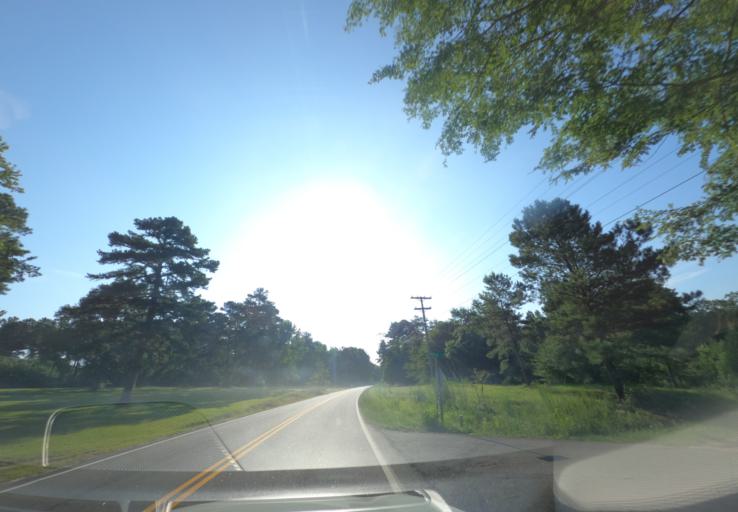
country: US
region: South Carolina
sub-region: Edgefield County
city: Murphys Estates
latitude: 33.5734
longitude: -82.0001
